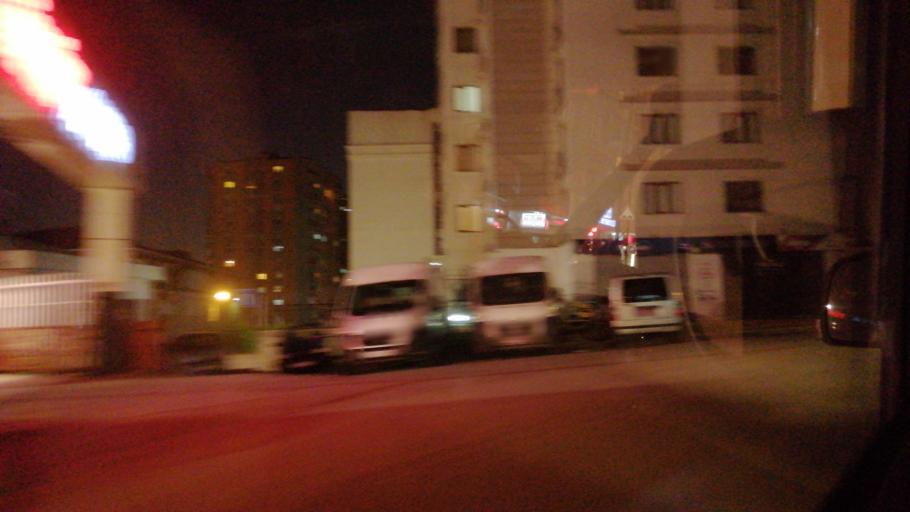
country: TR
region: Istanbul
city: Umraniye
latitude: 41.0177
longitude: 29.1282
